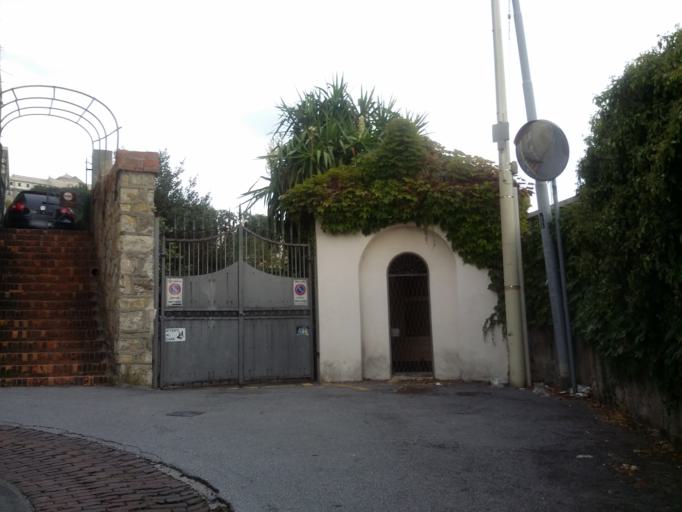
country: IT
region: Liguria
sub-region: Provincia di Genova
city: Genoa
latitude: 44.4105
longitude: 8.9624
